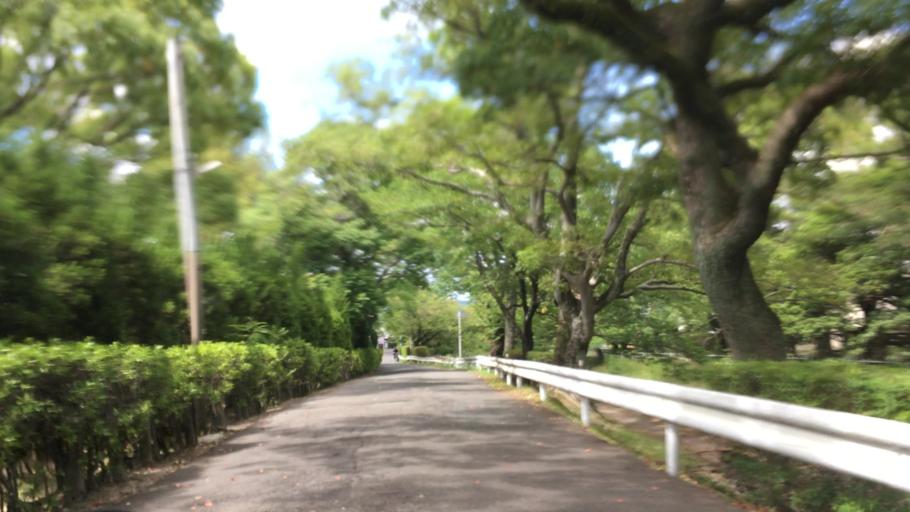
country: JP
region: Saga Prefecture
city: Saga-shi
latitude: 33.2655
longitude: 130.2829
